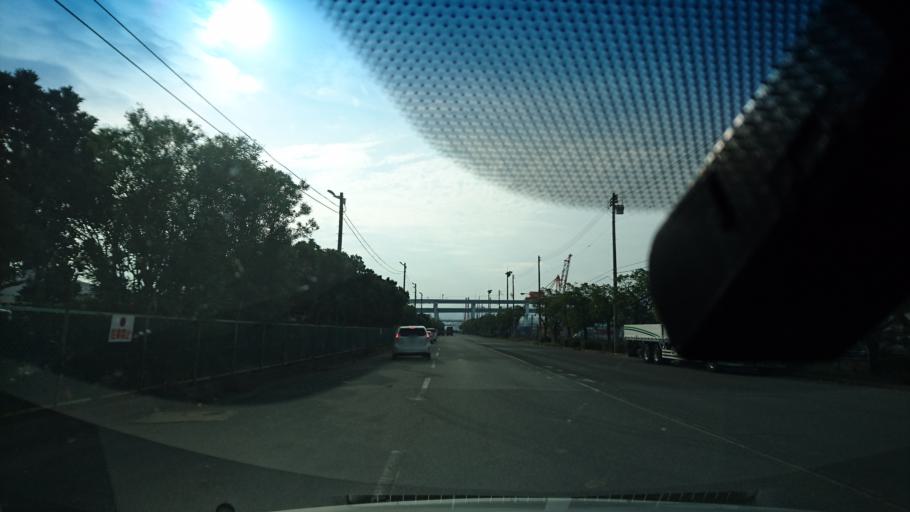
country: JP
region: Hyogo
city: Ashiya
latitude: 34.6970
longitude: 135.2797
